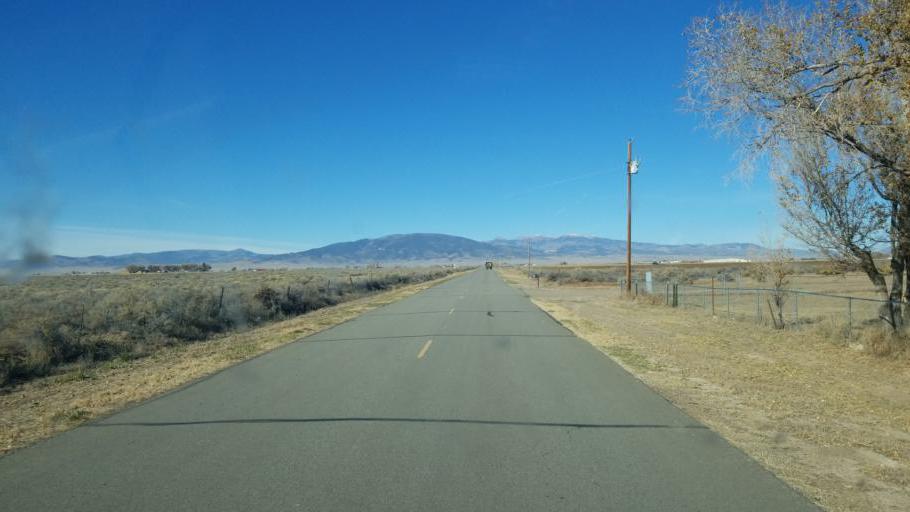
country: US
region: Colorado
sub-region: Alamosa County
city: Alamosa
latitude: 37.4586
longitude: -106.0216
